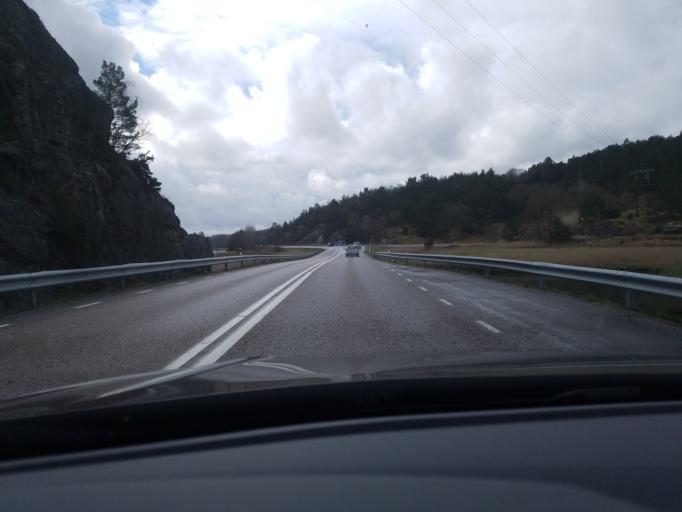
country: SE
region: Vaestra Goetaland
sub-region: Tjorns Kommun
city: Myggenas
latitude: 58.0770
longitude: 11.6964
